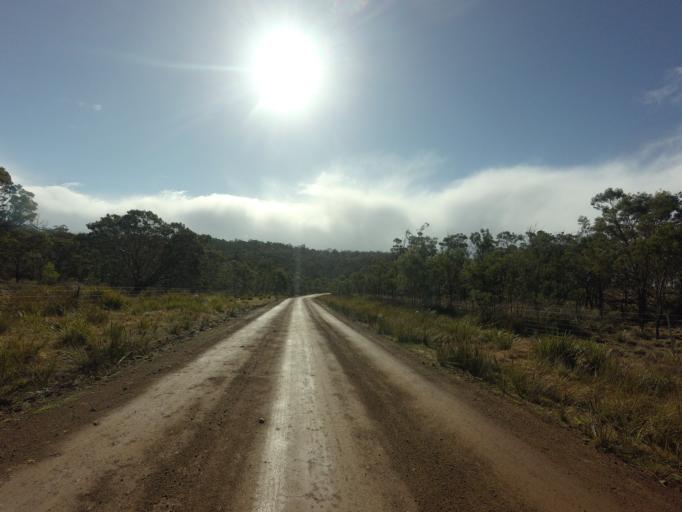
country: AU
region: Tasmania
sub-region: Sorell
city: Sorell
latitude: -42.4075
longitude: 147.9550
